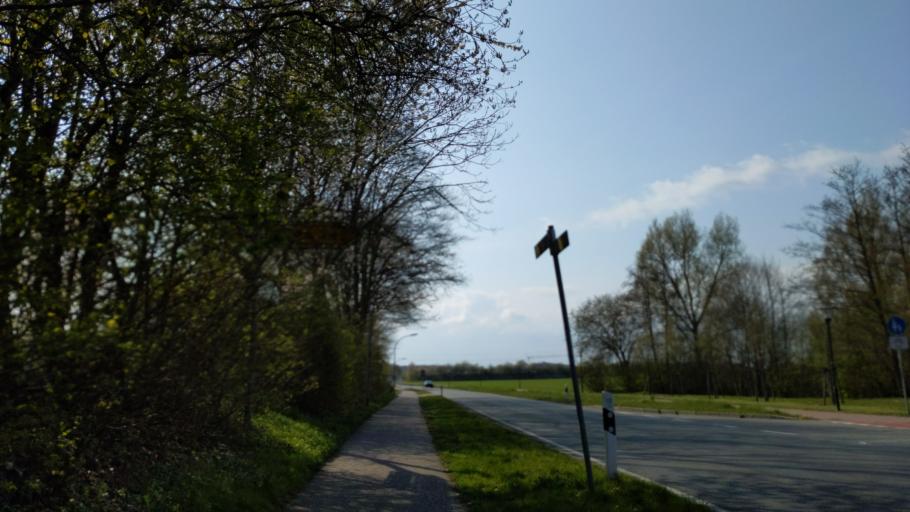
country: DE
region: Schleswig-Holstein
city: Bad Schwartau
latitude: 53.9207
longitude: 10.6750
